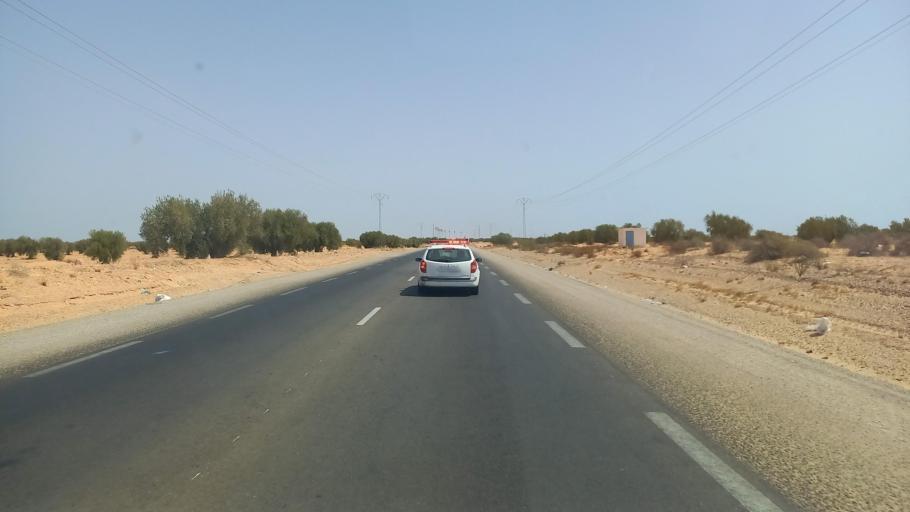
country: TN
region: Madanin
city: Zarzis
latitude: 33.4220
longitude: 10.8802
